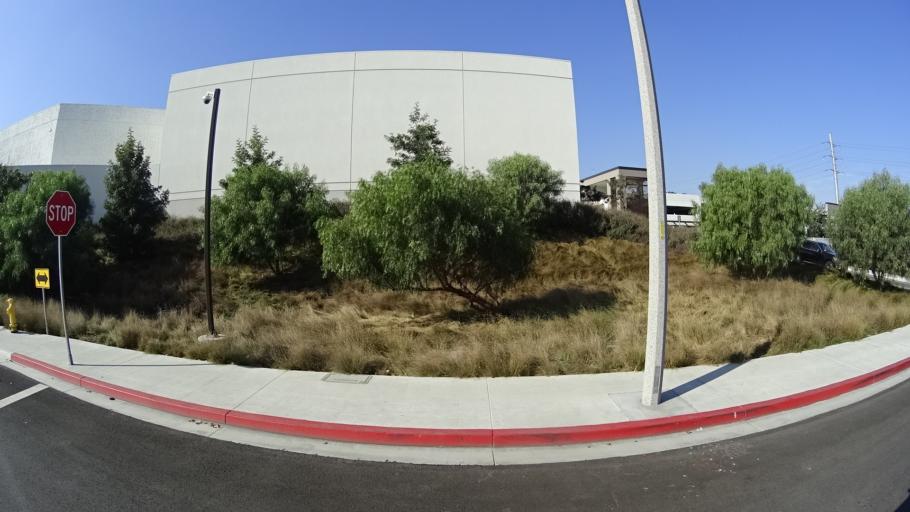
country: US
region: California
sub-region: Los Angeles County
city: Manhattan Beach
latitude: 33.9006
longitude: -118.3930
